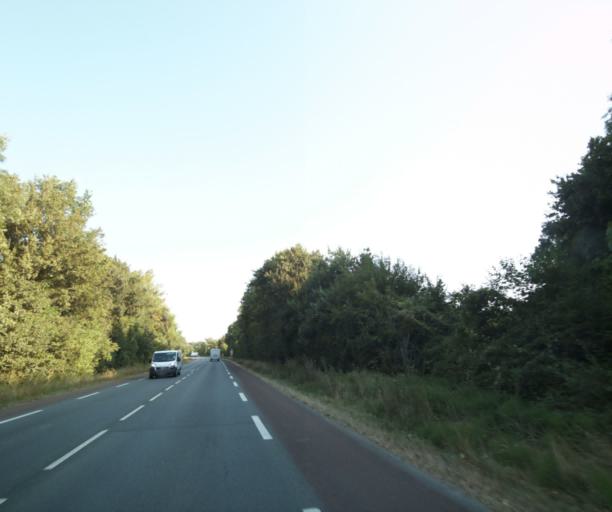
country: FR
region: Poitou-Charentes
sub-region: Departement de la Charente-Maritime
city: Cabariot
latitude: 45.9414
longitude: -0.8642
